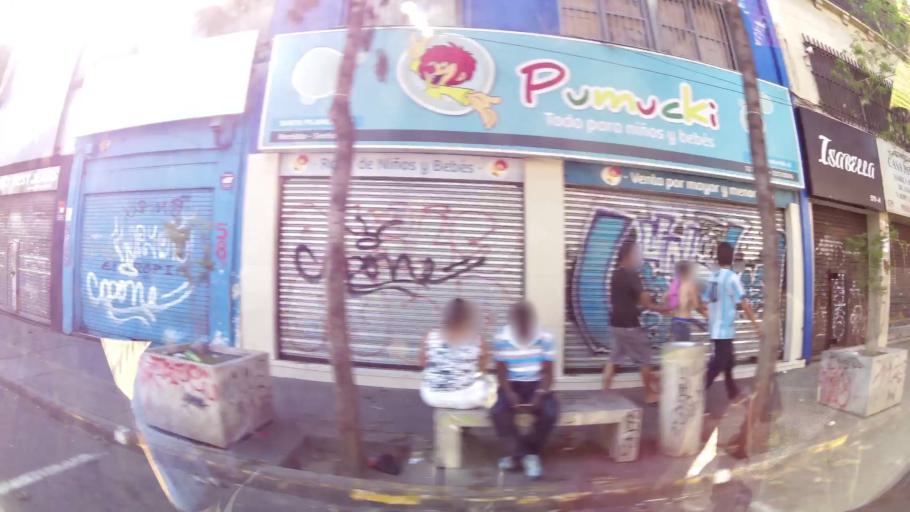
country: CL
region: Santiago Metropolitan
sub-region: Provincia de Santiago
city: Santiago
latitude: -33.4297
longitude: -70.6466
